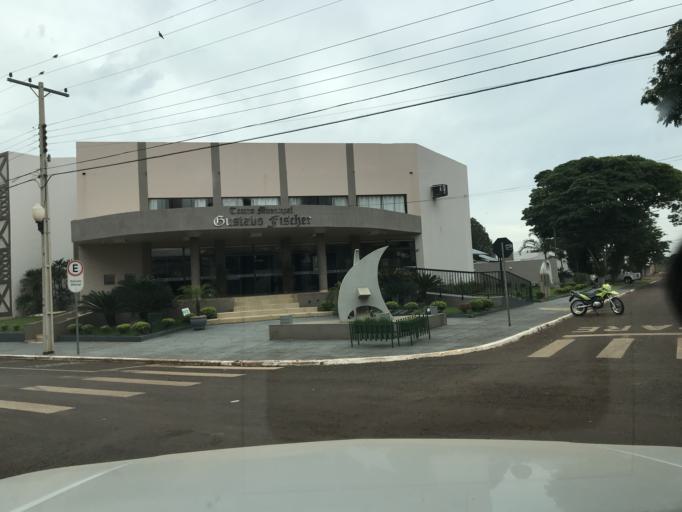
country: BR
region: Parana
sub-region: Marechal Candido Rondon
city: Marechal Candido Rondon
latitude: -24.4647
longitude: -53.9551
